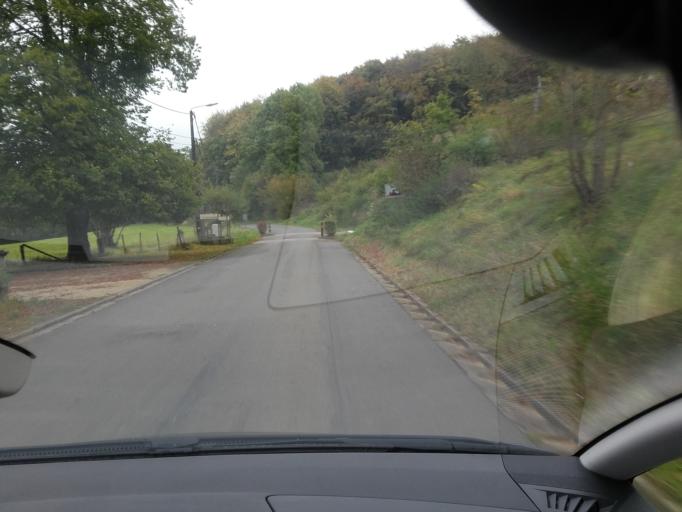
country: BE
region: Wallonia
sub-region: Province du Luxembourg
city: Attert
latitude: 49.7144
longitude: 5.7396
